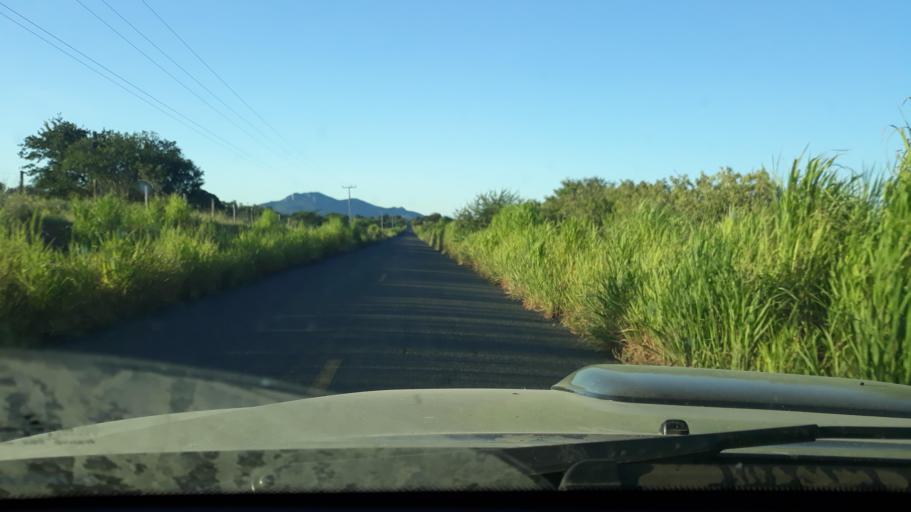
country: BR
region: Bahia
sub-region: Guanambi
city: Guanambi
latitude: -13.9751
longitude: -42.8550
